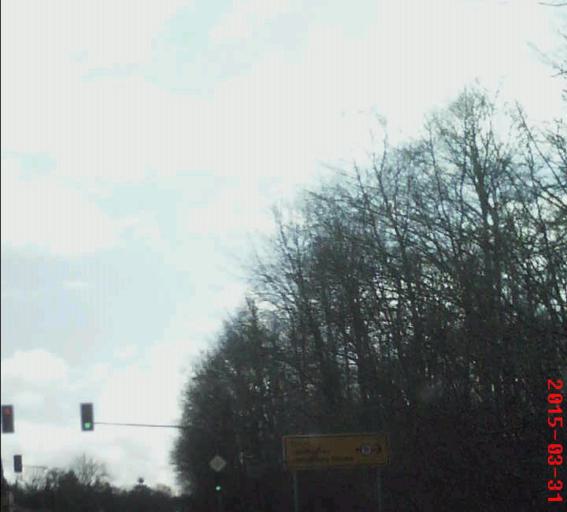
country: DE
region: Thuringia
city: Erfurt
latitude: 50.9446
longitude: 11.0323
